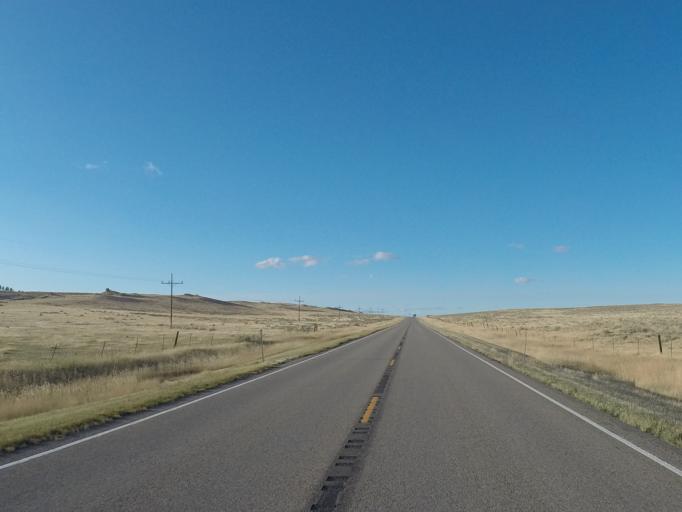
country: US
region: Montana
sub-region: Golden Valley County
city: Ryegate
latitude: 46.2343
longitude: -108.9333
